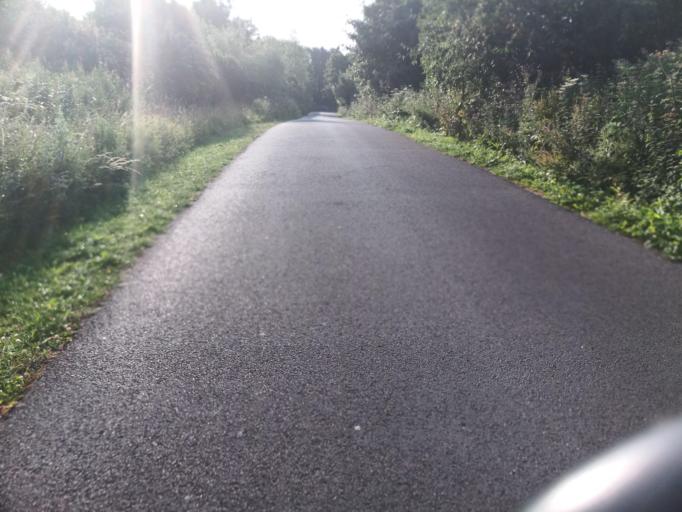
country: GB
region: Northern Ireland
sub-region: Castlereagh District
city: Dundonald
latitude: 54.5896
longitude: -5.8156
